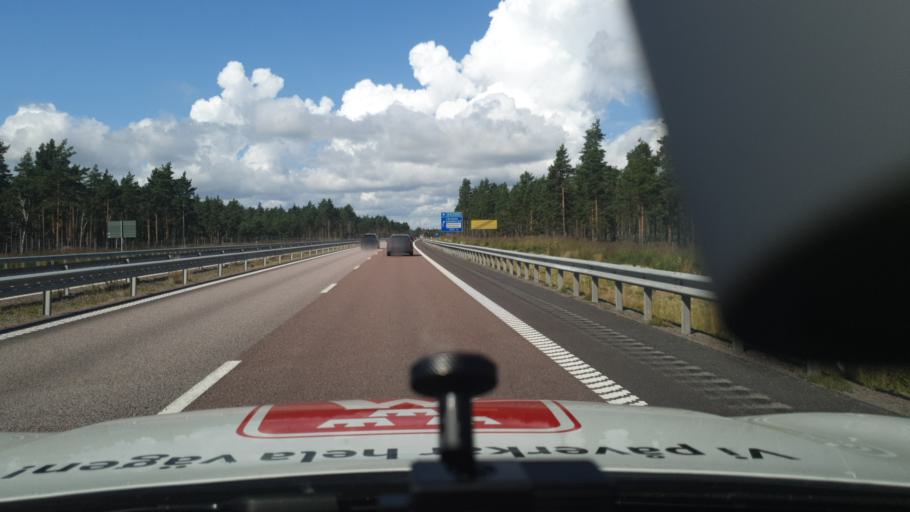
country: SE
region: Vaermland
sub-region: Kils Kommun
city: Kil
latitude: 59.3876
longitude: 13.3045
